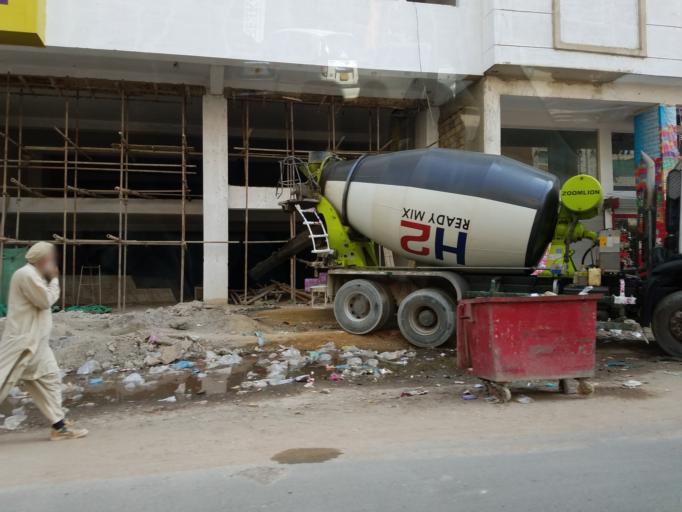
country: PK
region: Sindh
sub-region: Karachi District
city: Karachi
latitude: 24.8777
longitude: 67.0638
